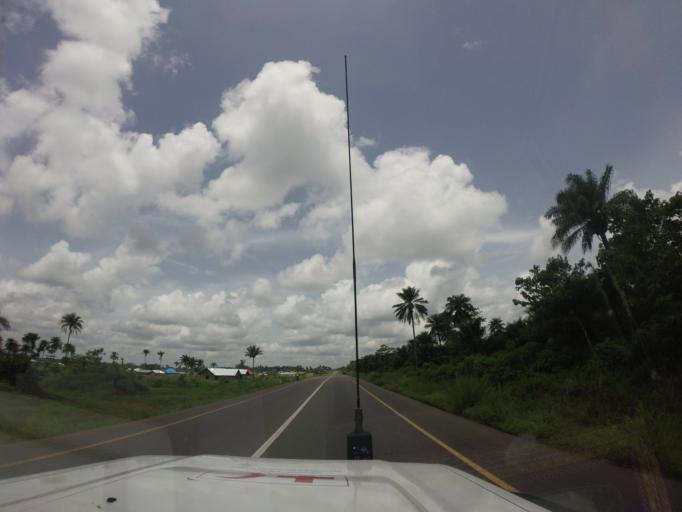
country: SL
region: Northern Province
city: Kambia
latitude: 9.0524
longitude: -12.9144
